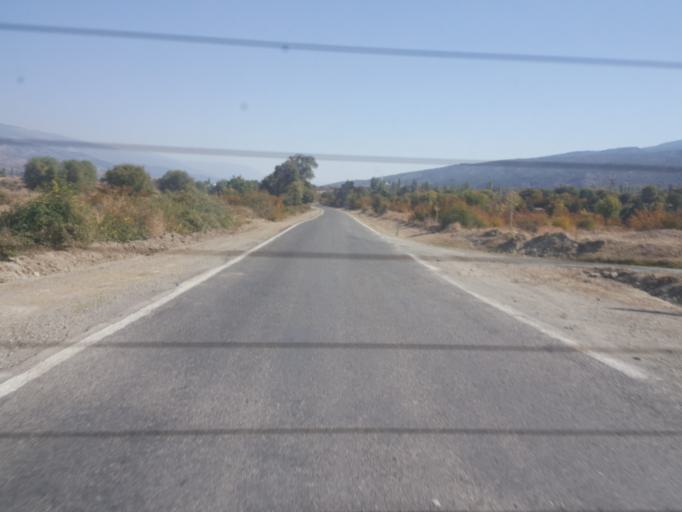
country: TR
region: Kastamonu
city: Tosya
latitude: 40.9975
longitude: 34.1409
